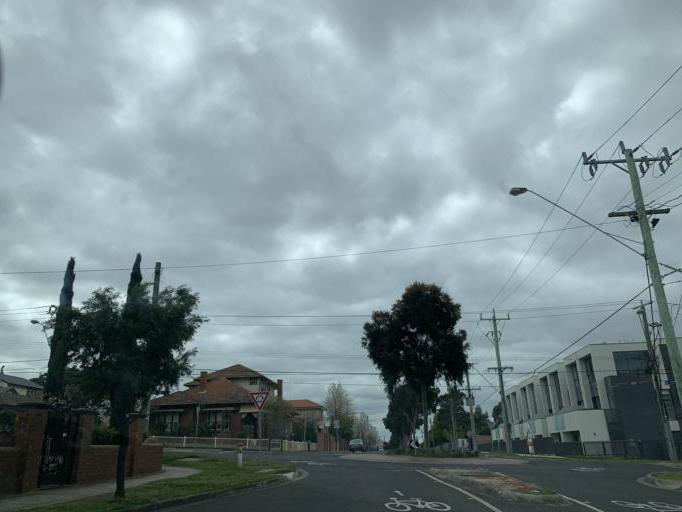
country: AU
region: Victoria
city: Thornbury
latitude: -37.7398
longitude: 144.9946
